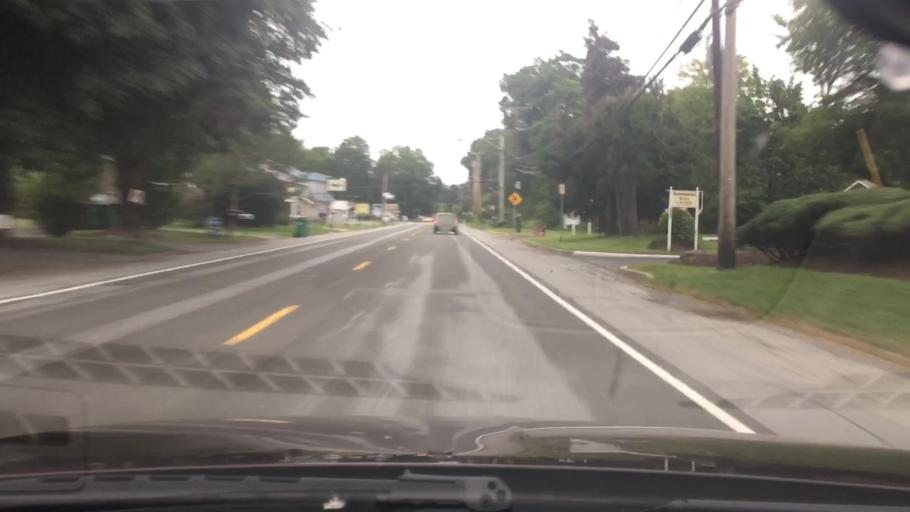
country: US
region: New York
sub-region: Dutchess County
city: Pleasant Valley
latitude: 41.7299
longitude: -73.8392
